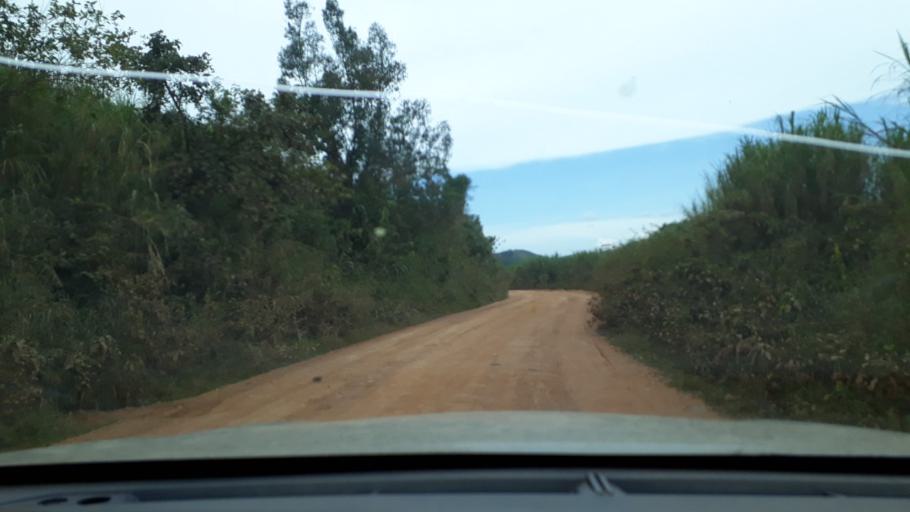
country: CD
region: Eastern Province
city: Bunia
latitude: 1.8253
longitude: 30.4447
